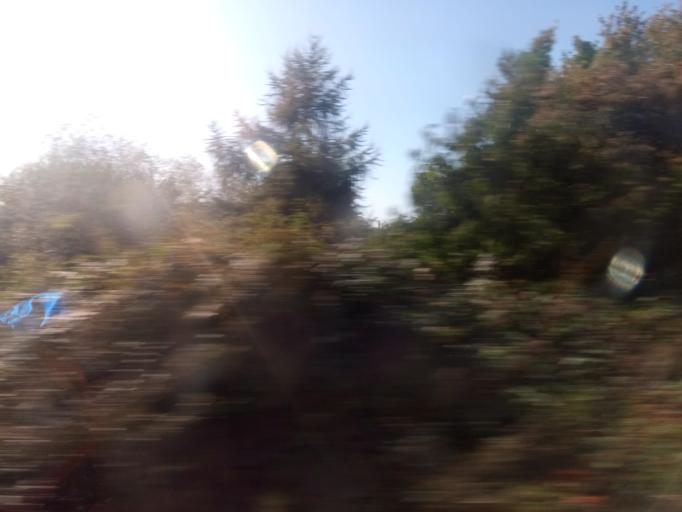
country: GB
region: England
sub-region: Cambridgeshire
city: Yaxley
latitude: 52.5194
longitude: -0.2405
